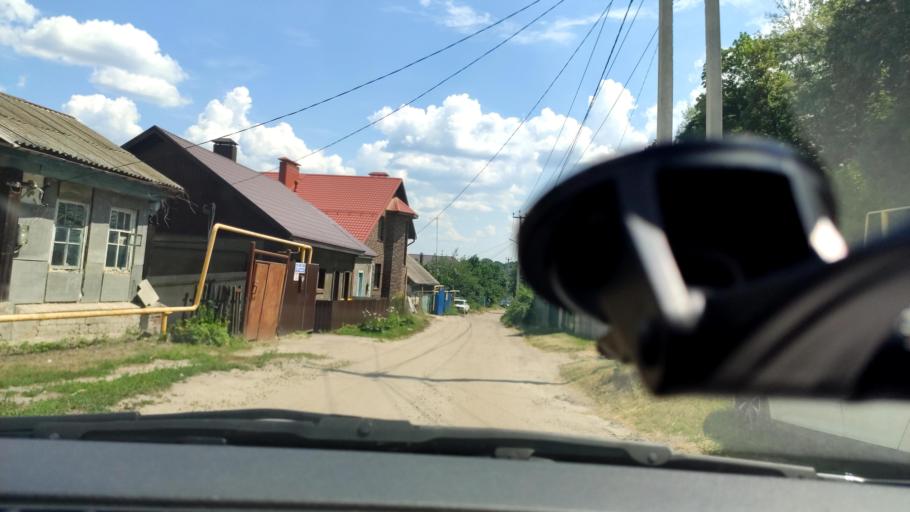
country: RU
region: Voronezj
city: Ramon'
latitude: 51.8952
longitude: 39.3406
